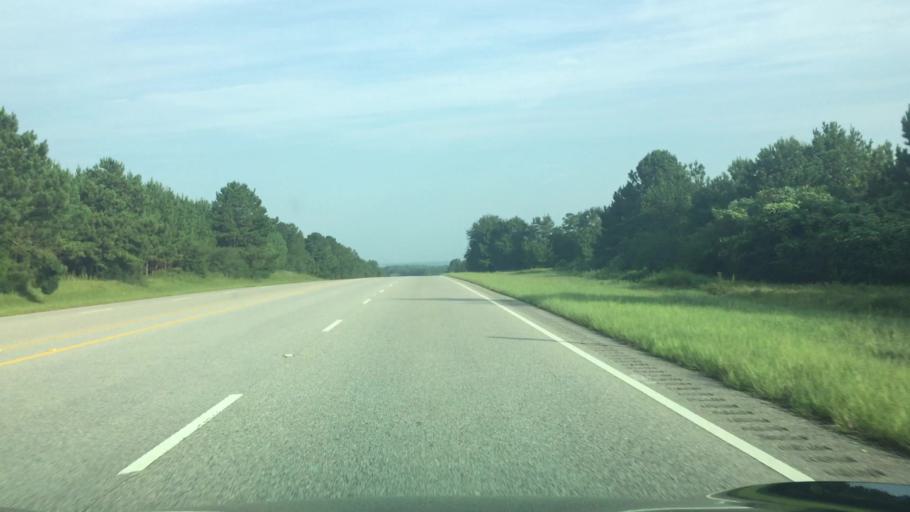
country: US
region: Alabama
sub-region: Covington County
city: Andalusia
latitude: 31.4531
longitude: -86.6307
